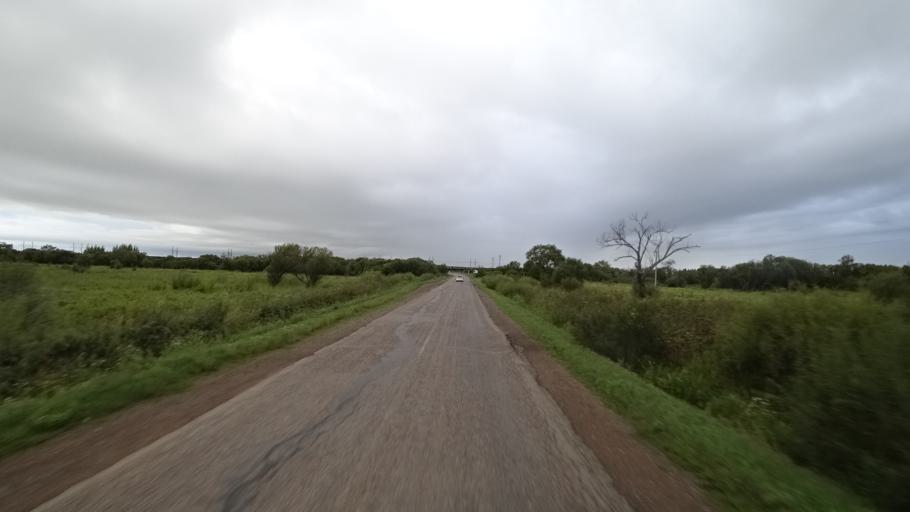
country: RU
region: Primorskiy
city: Chernigovka
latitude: 44.3617
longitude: 132.5543
